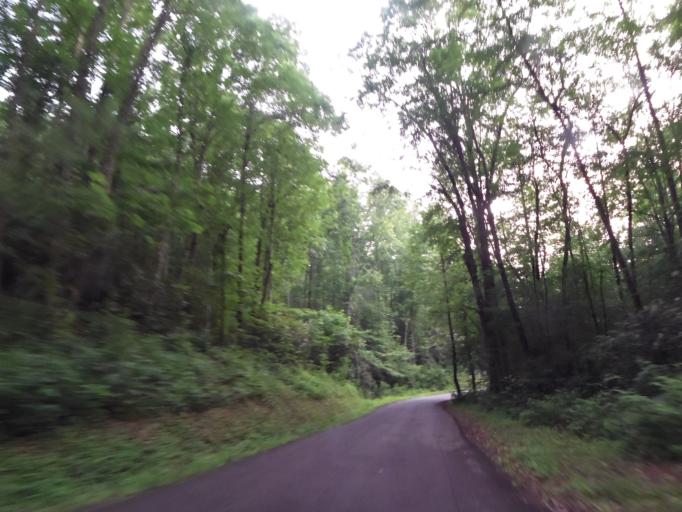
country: US
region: Tennessee
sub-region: Sevier County
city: Seymour
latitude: 35.7451
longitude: -83.7300
